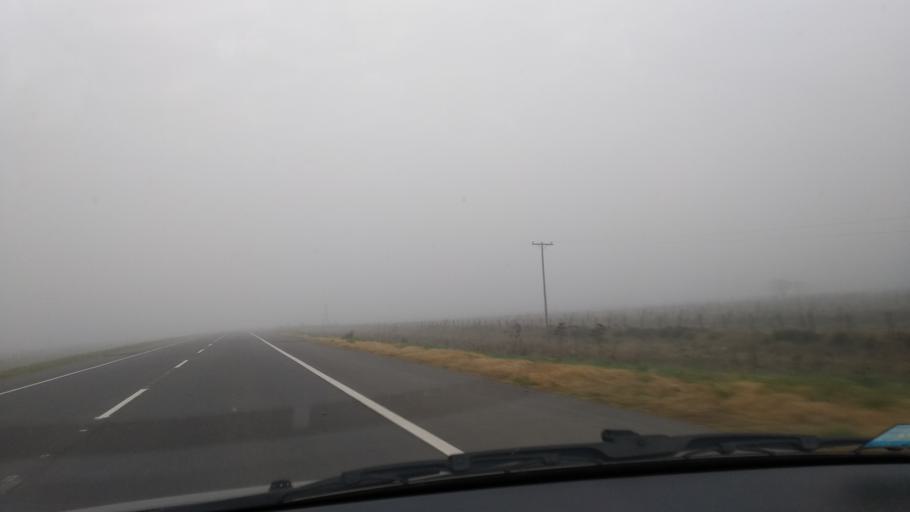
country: AR
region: Buenos Aires
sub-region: Partido de Brandsen
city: Brandsen
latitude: -35.1943
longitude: -58.3746
